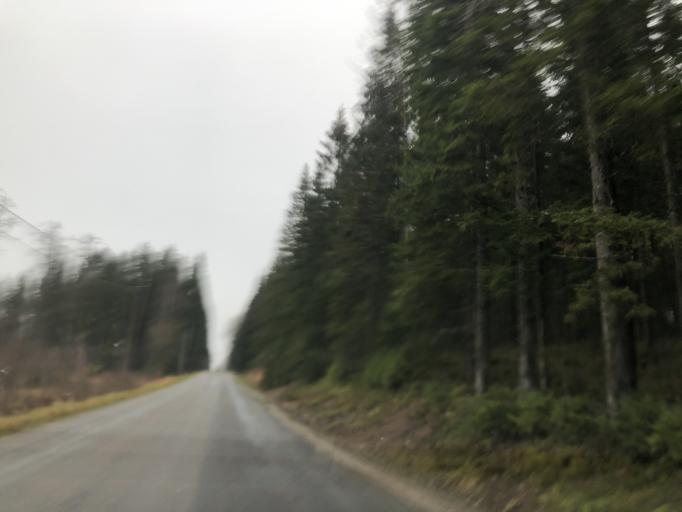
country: SE
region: Vaestra Goetaland
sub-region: Ulricehamns Kommun
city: Ulricehamn
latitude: 57.7081
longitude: 13.5093
